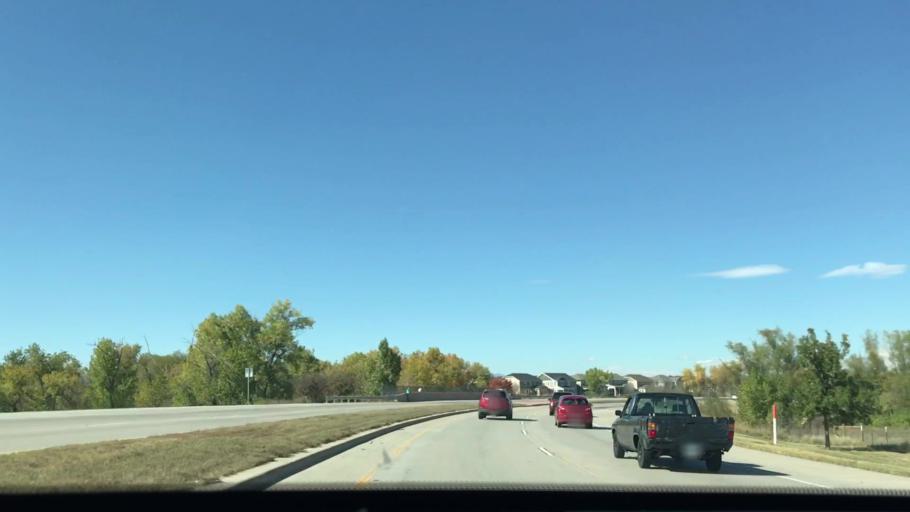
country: US
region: Colorado
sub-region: Boulder County
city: Lafayette
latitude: 39.9790
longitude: -105.0969
